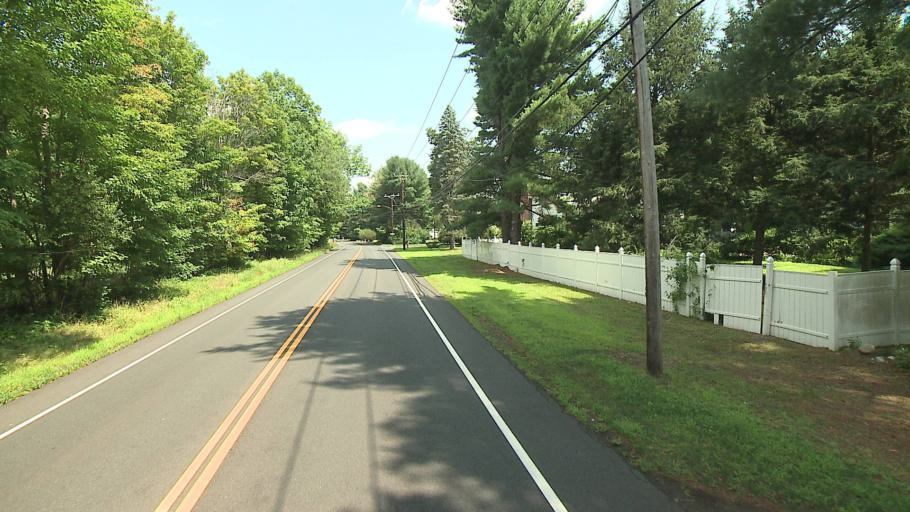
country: US
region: Connecticut
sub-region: Hartford County
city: Canton Valley
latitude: 41.8078
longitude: -72.8875
